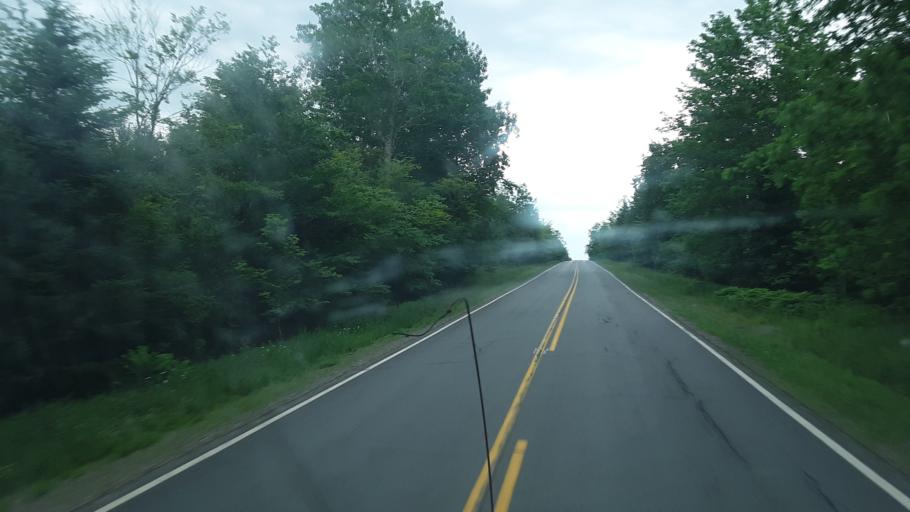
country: US
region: Maine
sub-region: Penobscot County
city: Medway
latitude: 45.7214
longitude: -68.2965
